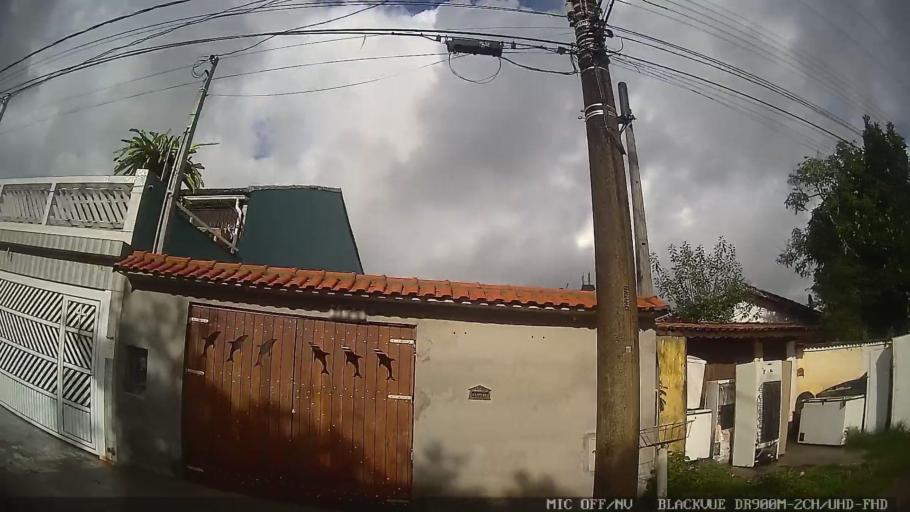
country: BR
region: Sao Paulo
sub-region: Itanhaem
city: Itanhaem
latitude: -24.2253
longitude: -46.8904
